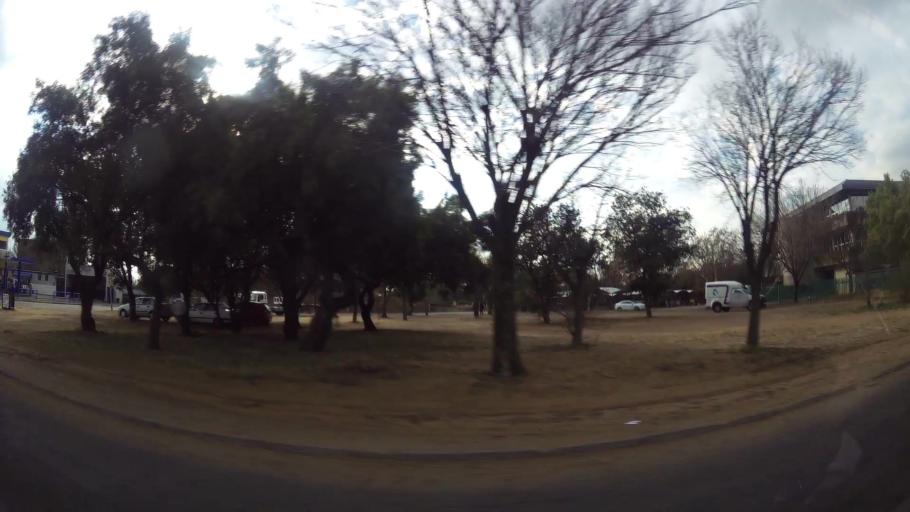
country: ZA
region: Orange Free State
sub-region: Fezile Dabi District Municipality
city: Sasolburg
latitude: -26.8186
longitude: 27.8287
